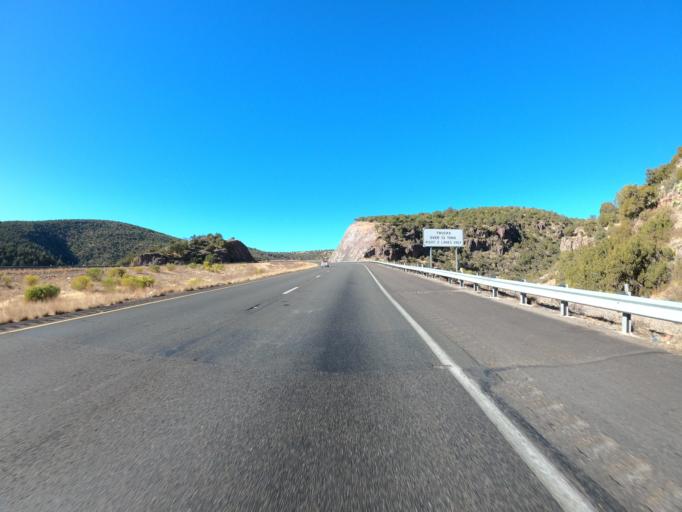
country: US
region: Arizona
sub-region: Yavapai County
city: Camp Verde
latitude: 34.5313
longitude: -111.9449
